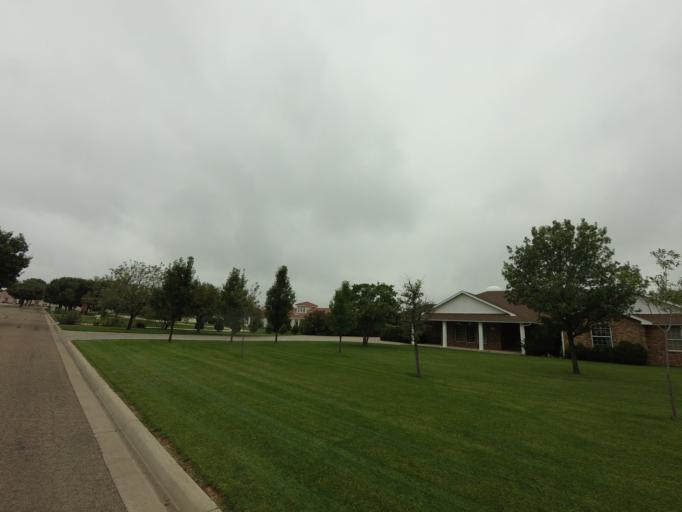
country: US
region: New Mexico
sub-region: Curry County
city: Clovis
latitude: 34.4323
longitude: -103.1835
